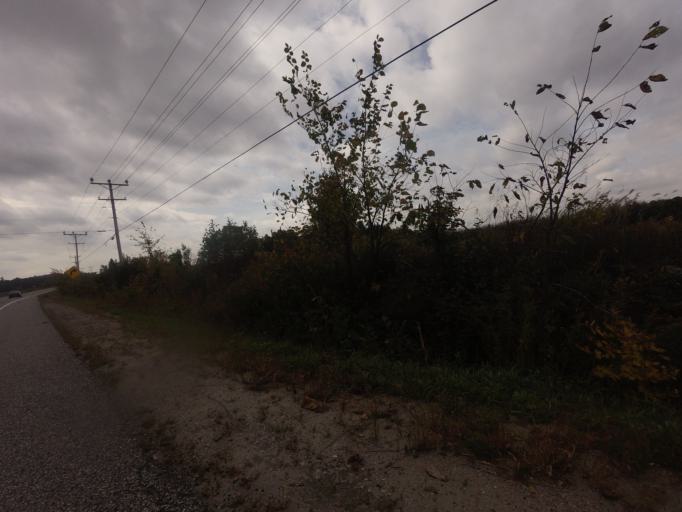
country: CA
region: Quebec
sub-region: Outaouais
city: Wakefield
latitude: 45.9003
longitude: -76.0253
